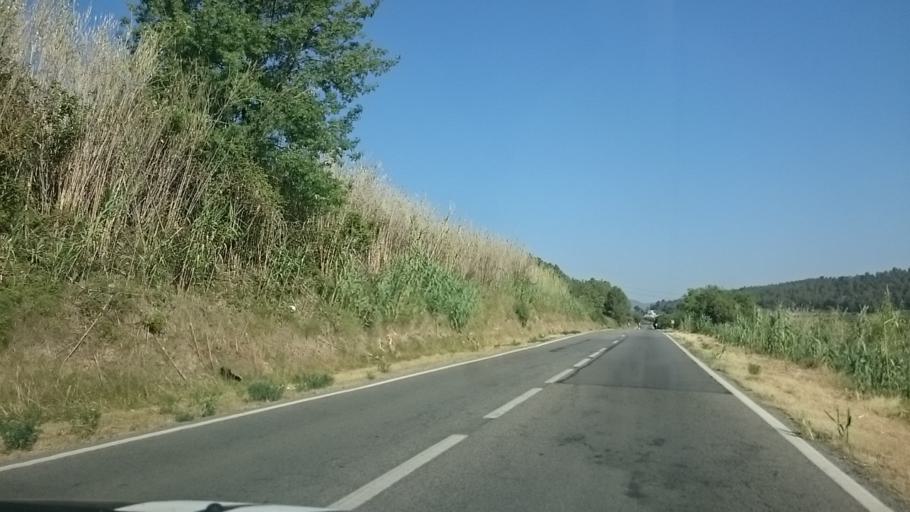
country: ES
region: Catalonia
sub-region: Provincia de Barcelona
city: Vilobi del Penedes
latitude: 41.3758
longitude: 1.6457
